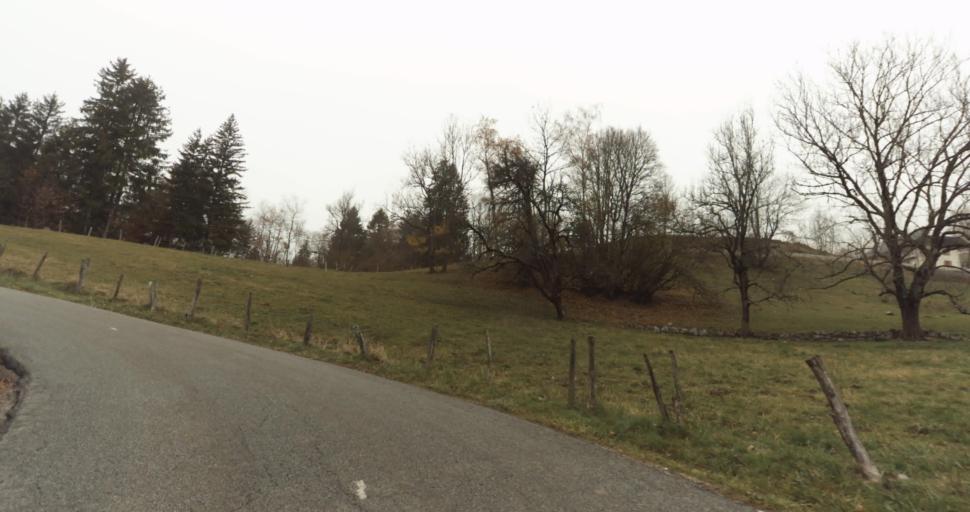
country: FR
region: Rhone-Alpes
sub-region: Departement de la Haute-Savoie
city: Doussard
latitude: 45.7971
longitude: 6.2609
